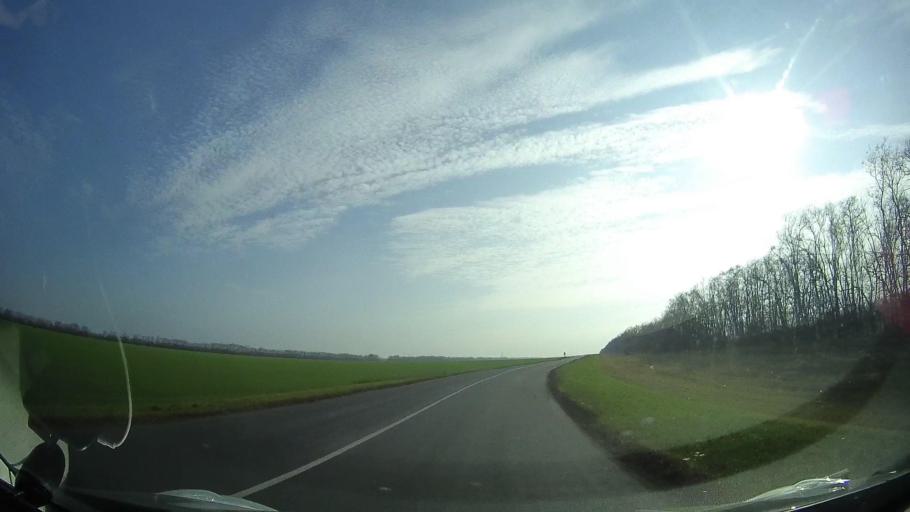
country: RU
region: Rostov
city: Mechetinskaya
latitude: 46.9030
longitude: 40.5414
